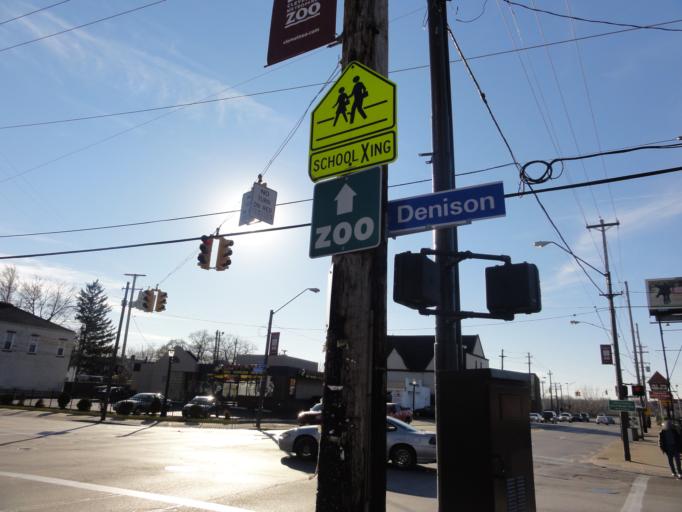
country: US
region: Ohio
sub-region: Cuyahoga County
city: Brooklyn Heights
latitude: 41.4512
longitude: -81.7019
